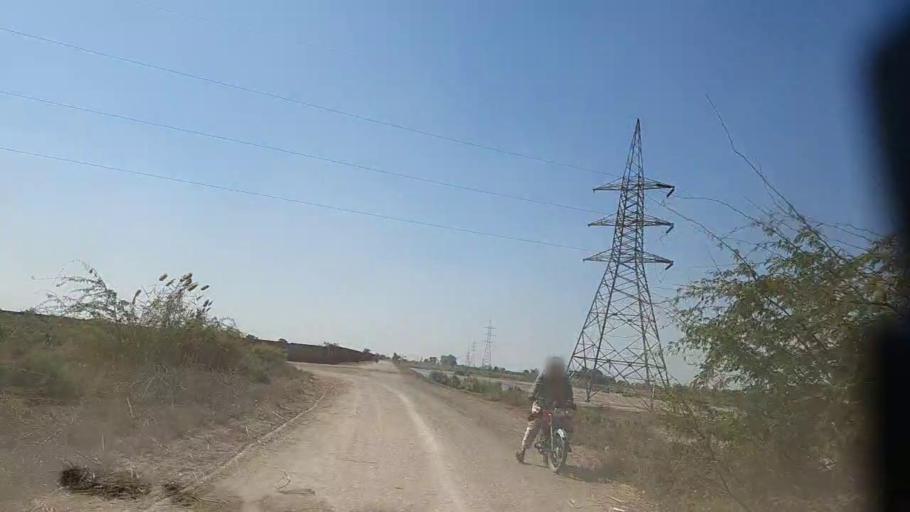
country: PK
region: Sindh
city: Digri
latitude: 25.1658
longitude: 69.0365
